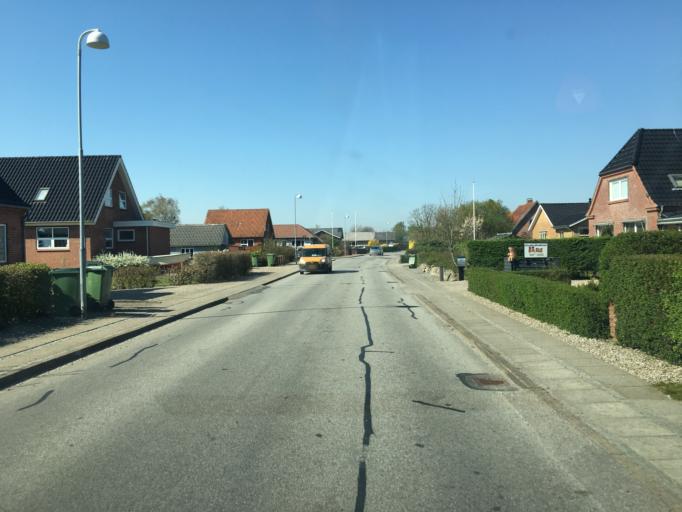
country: DK
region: South Denmark
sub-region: Aabenraa Kommune
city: Rodekro
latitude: 55.0269
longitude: 9.3068
